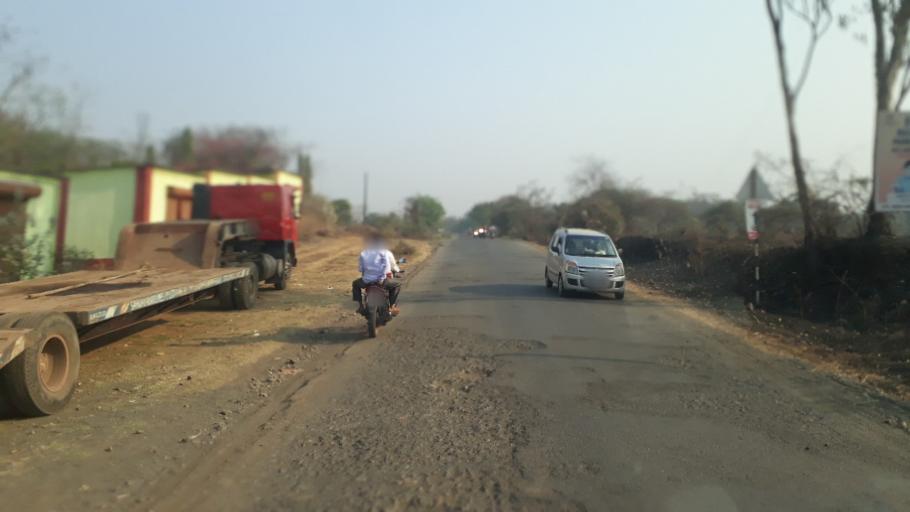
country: IN
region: Maharashtra
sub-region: Raigarh
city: Neral
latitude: 19.0449
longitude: 73.3319
